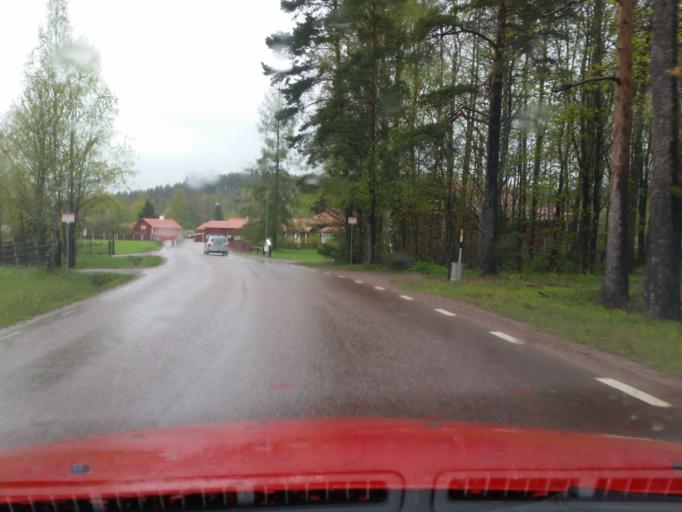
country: SE
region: Dalarna
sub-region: Saters Kommun
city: Saeter
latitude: 60.3425
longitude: 15.7840
